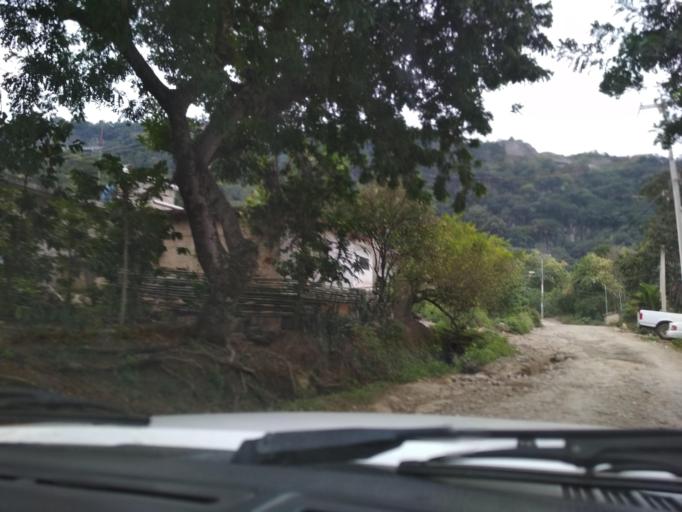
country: MX
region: Veracruz
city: El Castillo
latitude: 19.5832
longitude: -96.8714
